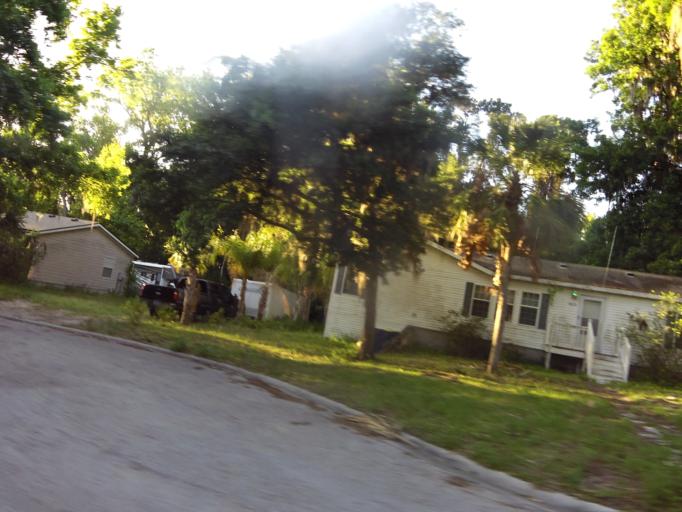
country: US
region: Florida
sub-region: Duval County
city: Atlantic Beach
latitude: 30.3685
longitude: -81.5169
